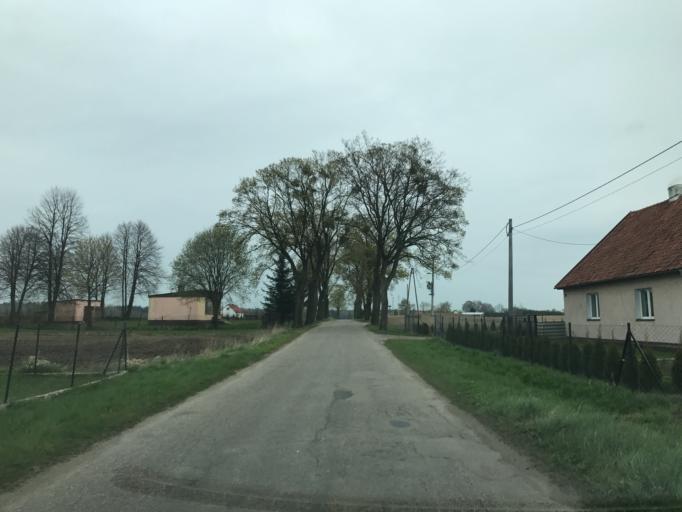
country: PL
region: Warmian-Masurian Voivodeship
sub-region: Powiat olsztynski
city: Olsztynek
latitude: 53.6305
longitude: 20.1759
